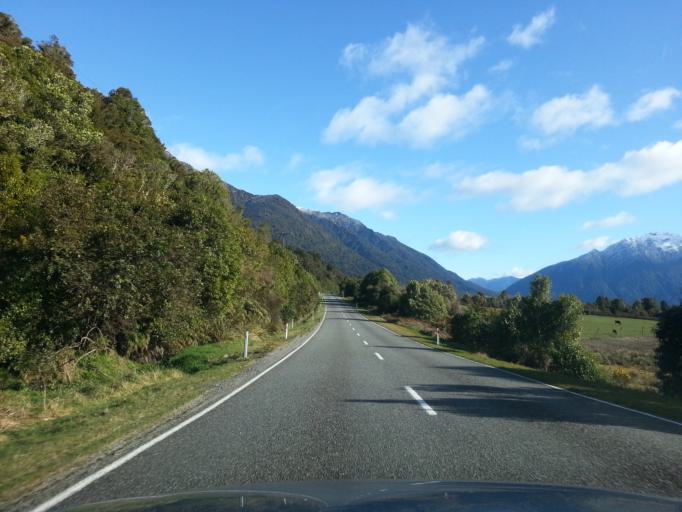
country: NZ
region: West Coast
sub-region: Grey District
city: Greymouth
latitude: -42.7424
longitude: 171.4234
